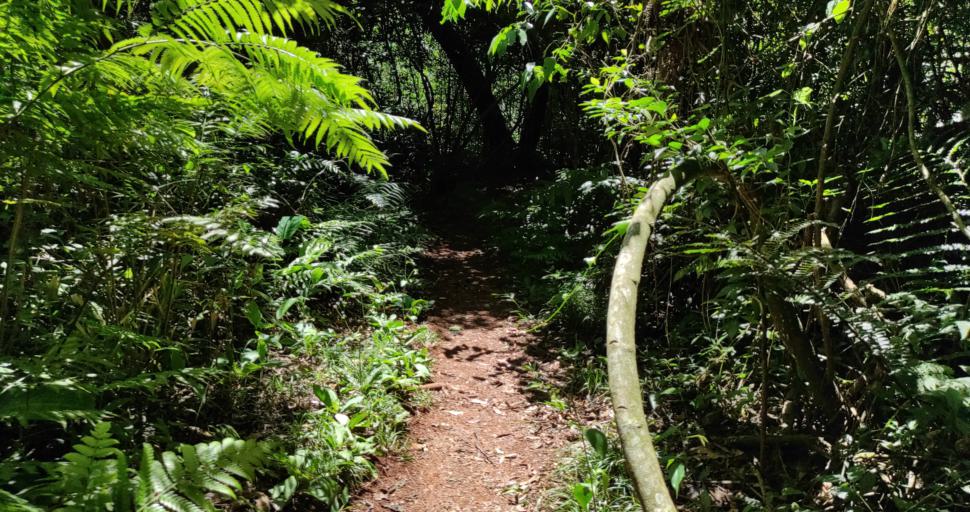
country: BR
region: Rio Grande do Sul
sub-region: Tres Passos
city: Tres Passos
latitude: -27.1491
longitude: -53.8989
